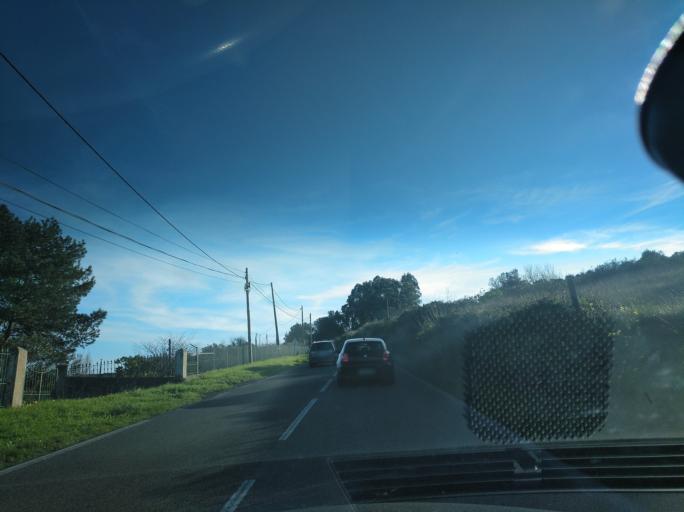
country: PT
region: Lisbon
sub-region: Sintra
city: Pero Pinheiro
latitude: 38.8818
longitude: -9.3300
